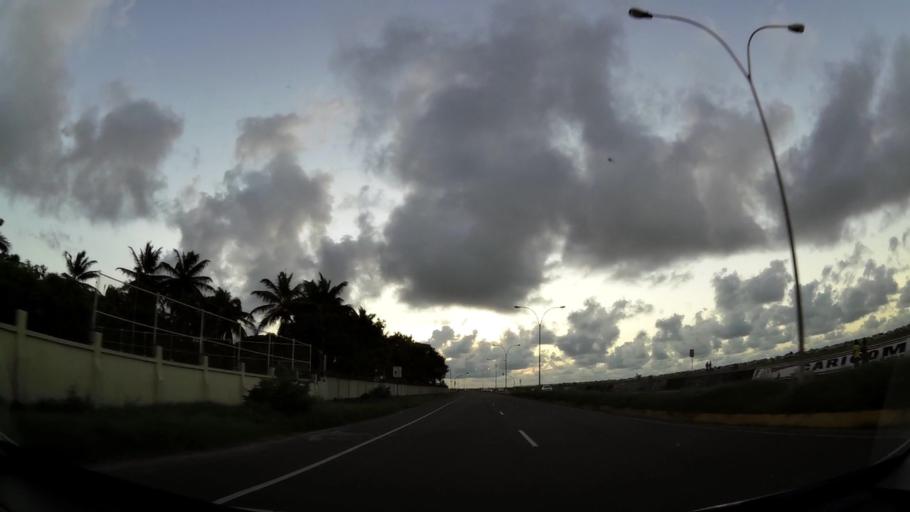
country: GY
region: Demerara-Mahaica
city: Georgetown
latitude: 6.8244
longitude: -58.1094
